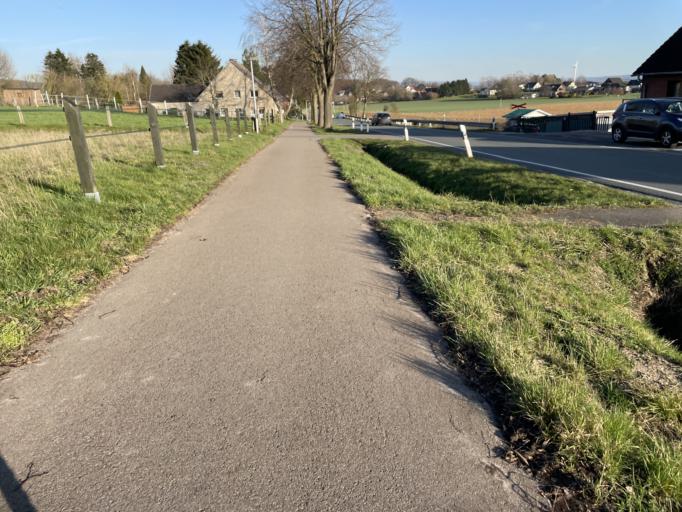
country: DE
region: North Rhine-Westphalia
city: Porta Westfalica
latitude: 52.2297
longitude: 8.9513
